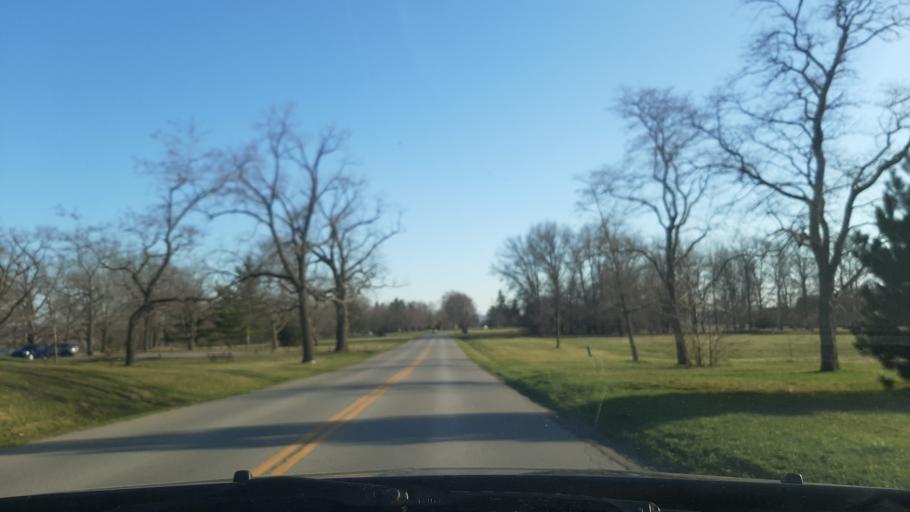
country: US
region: New York
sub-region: Niagara County
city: Youngstown
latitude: 43.2375
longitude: -79.0610
